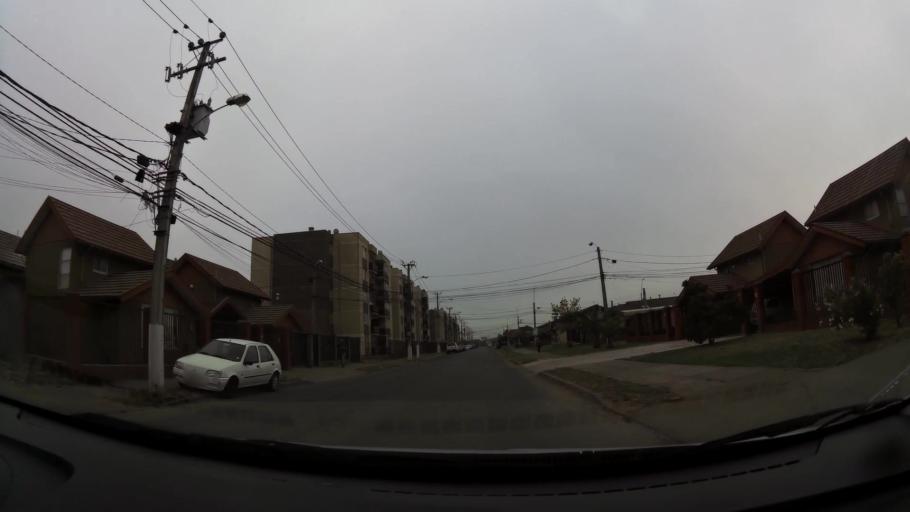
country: CL
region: Biobio
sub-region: Provincia de Concepcion
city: Concepcion
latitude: -36.7883
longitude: -73.0810
